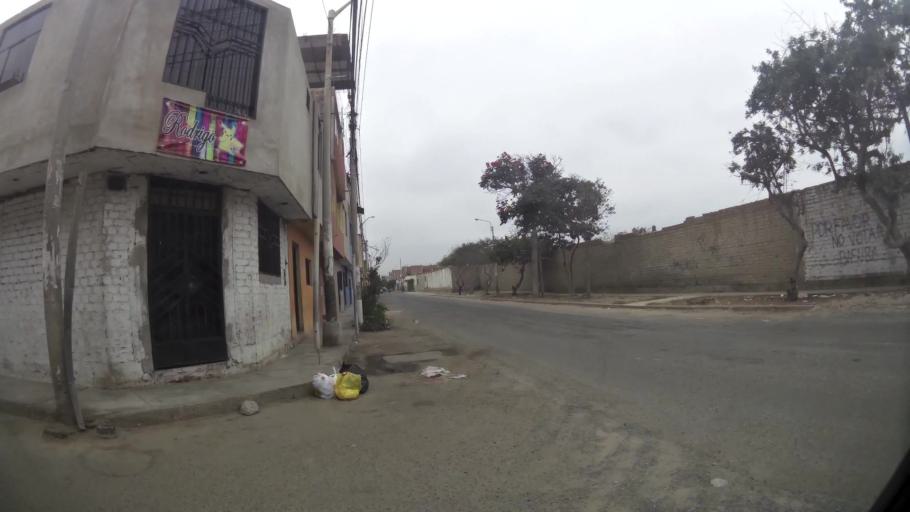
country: PE
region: La Libertad
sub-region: Provincia de Trujillo
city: Trujillo
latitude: -8.1074
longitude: -79.0419
